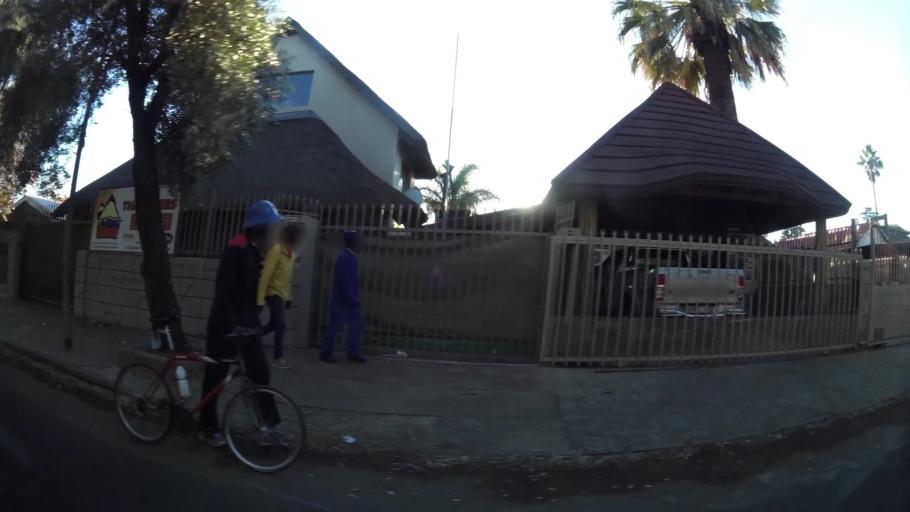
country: ZA
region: Northern Cape
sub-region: Frances Baard District Municipality
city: Kimberley
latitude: -28.7527
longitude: 24.7358
